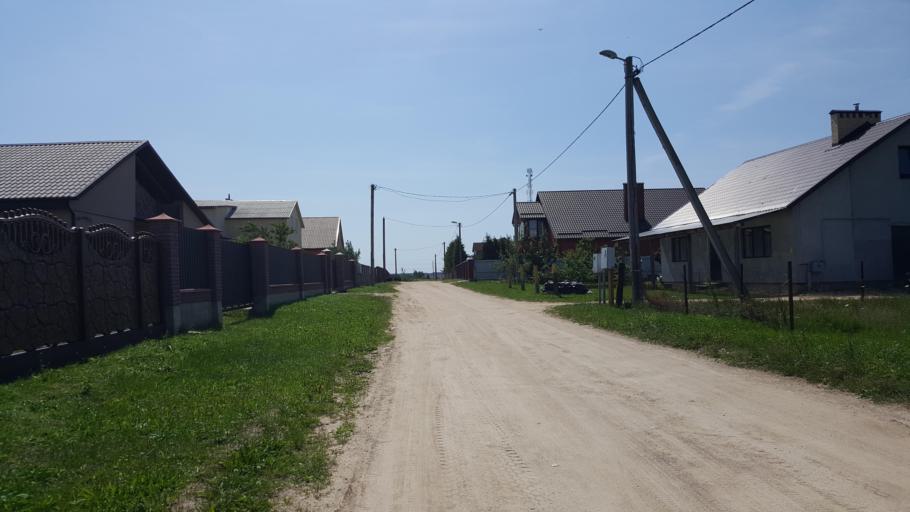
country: BY
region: Brest
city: Vysokaye
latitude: 52.3602
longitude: 23.3913
